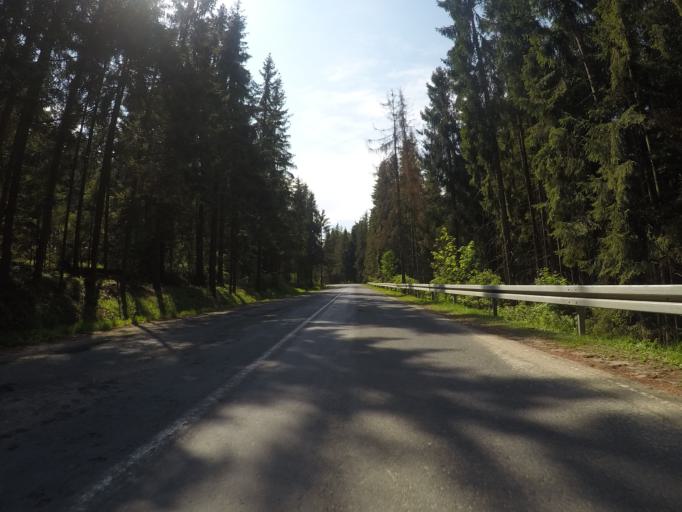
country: PL
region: Lesser Poland Voivodeship
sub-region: Powiat tatrzanski
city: Bukowina Tatrzanska
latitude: 49.3167
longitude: 20.1064
